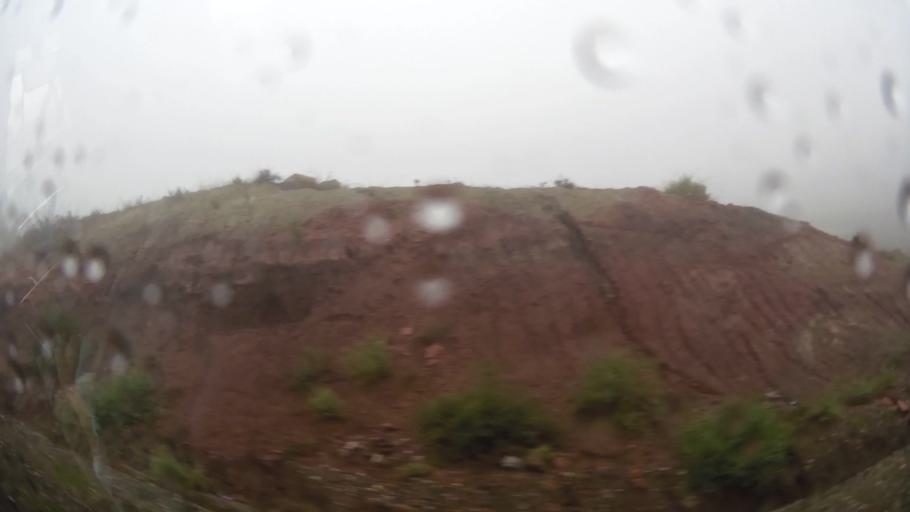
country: MA
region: Taza-Al Hoceima-Taounate
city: Tirhanimine
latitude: 35.2332
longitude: -3.9711
